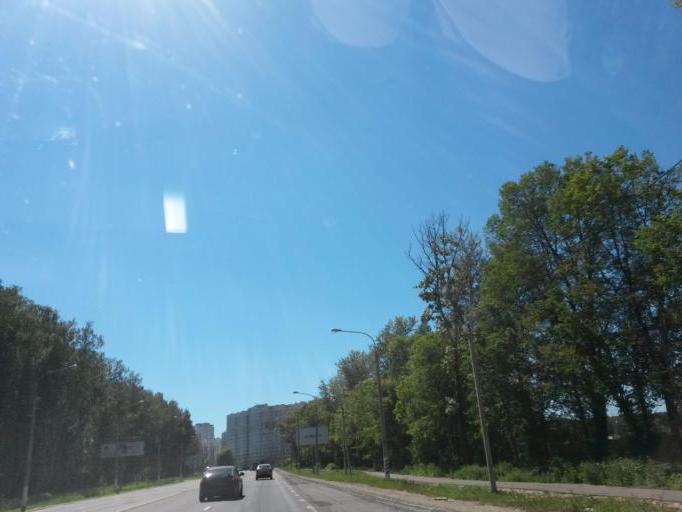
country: RU
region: Moskovskaya
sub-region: Chekhovskiy Rayon
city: Chekhov
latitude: 55.1752
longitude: 37.4764
